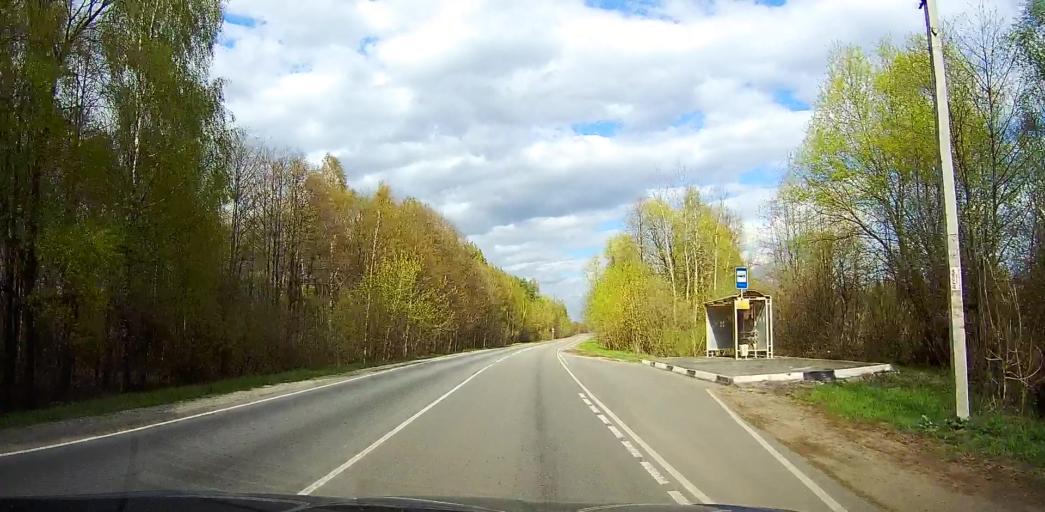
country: RU
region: Moskovskaya
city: Rakhmanovo
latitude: 55.7355
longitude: 38.6349
